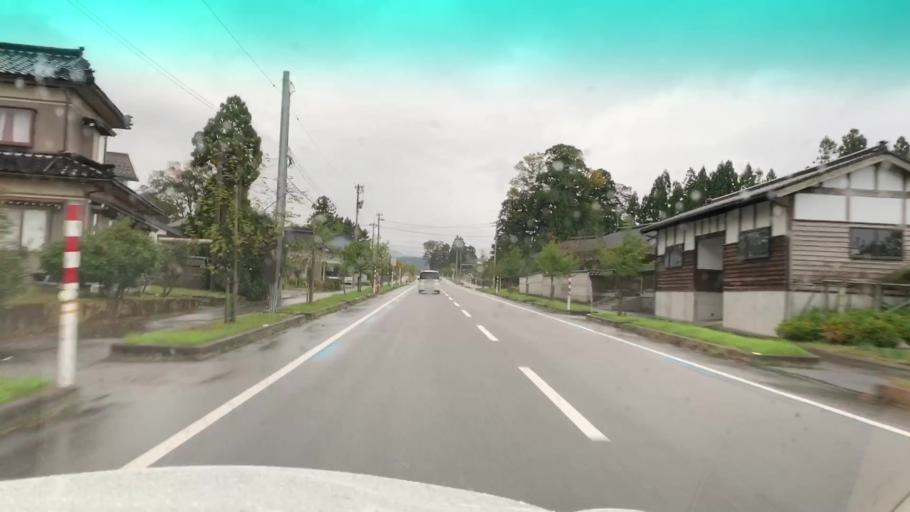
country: JP
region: Toyama
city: Kamiichi
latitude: 36.6156
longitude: 137.3261
